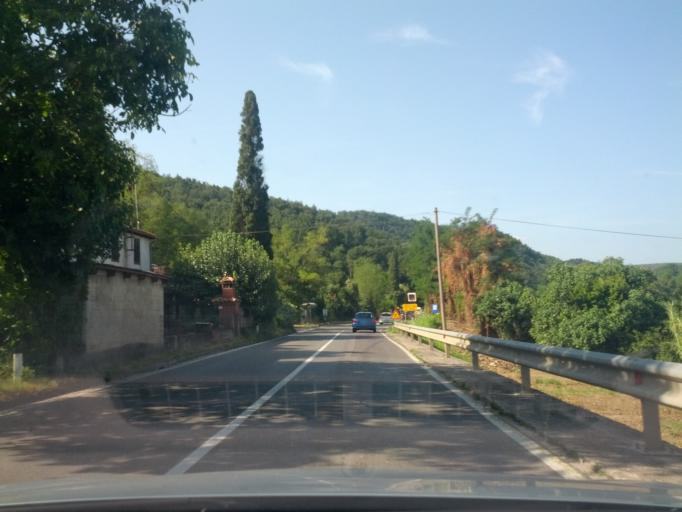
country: SI
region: Izola-Isola
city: Jagodje
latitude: 45.4727
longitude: 13.6731
